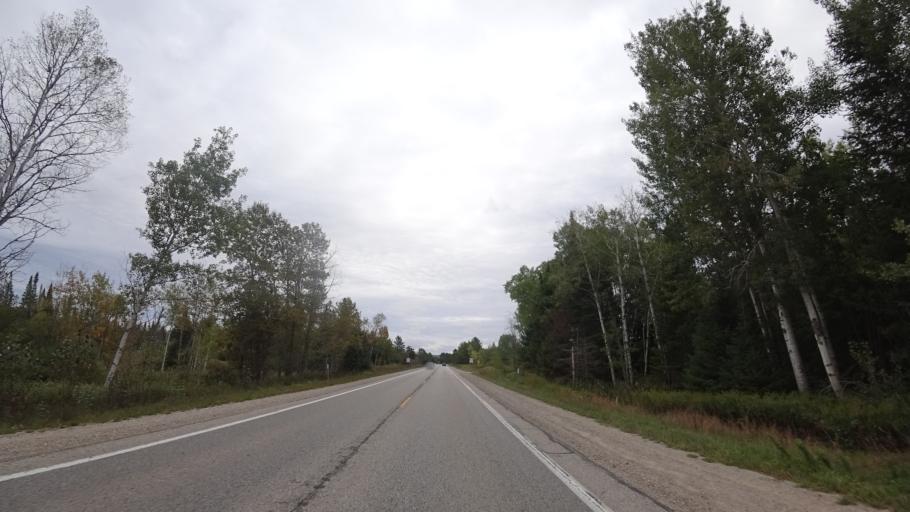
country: US
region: Michigan
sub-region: Charlevoix County
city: Boyne City
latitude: 45.1974
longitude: -84.9207
